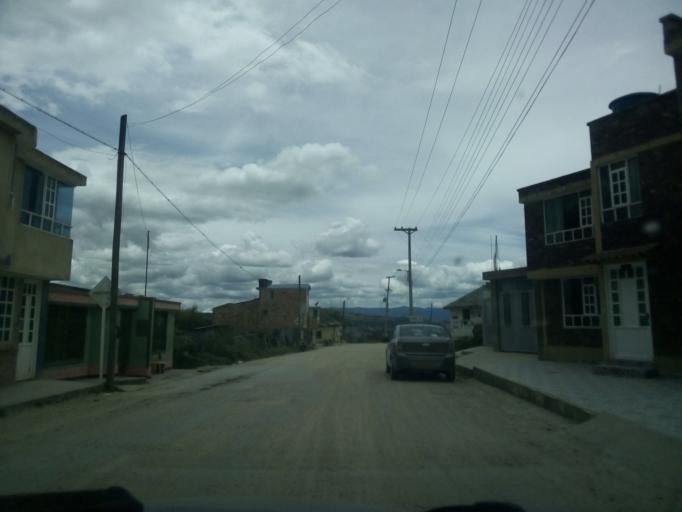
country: CO
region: Boyaca
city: Toca
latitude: 5.5687
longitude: -73.1831
